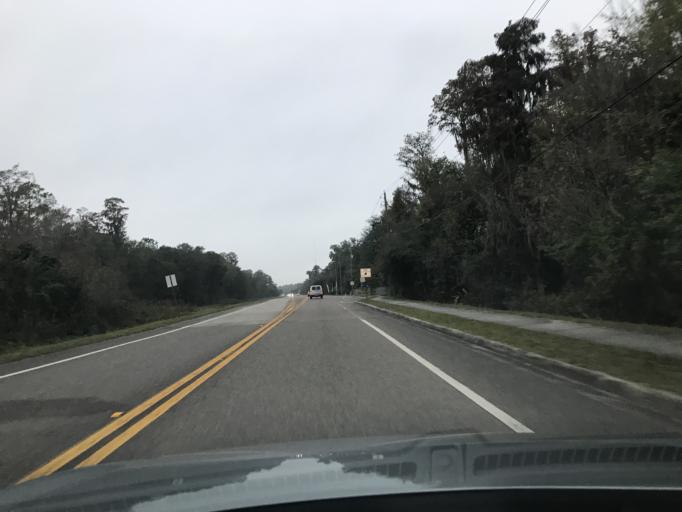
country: US
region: Florida
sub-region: Hillsborough County
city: Westchase
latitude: 28.0562
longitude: -82.6305
